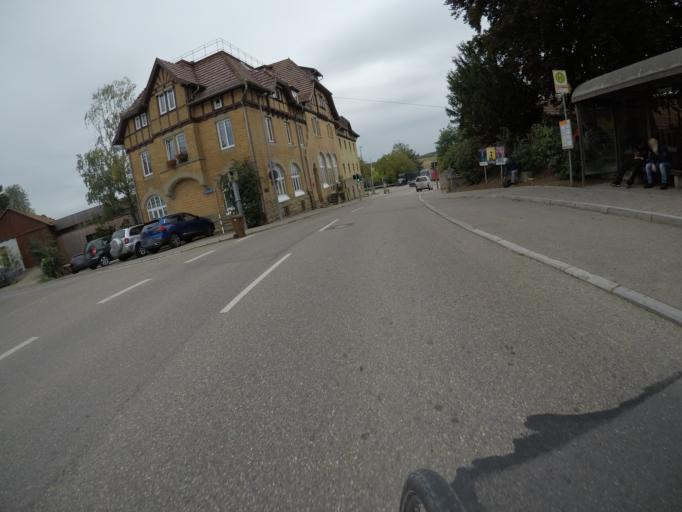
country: DE
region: Baden-Wuerttemberg
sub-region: Regierungsbezirk Stuttgart
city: Eberdingen
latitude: 48.8520
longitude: 8.9866
